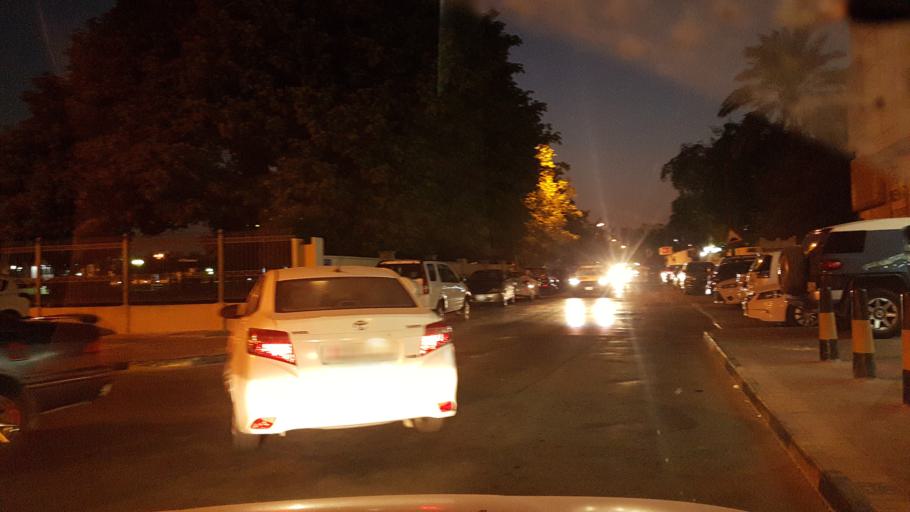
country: BH
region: Manama
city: Manama
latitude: 26.2222
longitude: 50.5843
